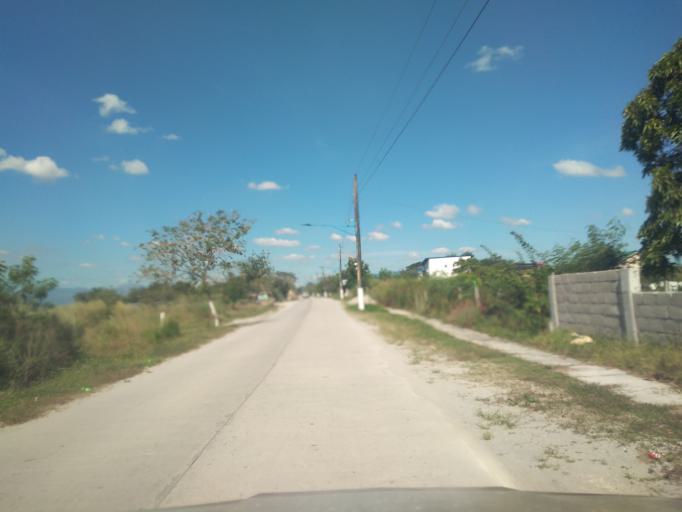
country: PH
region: Central Luzon
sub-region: Province of Pampanga
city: San Basilio
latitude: 15.0374
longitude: 120.6200
